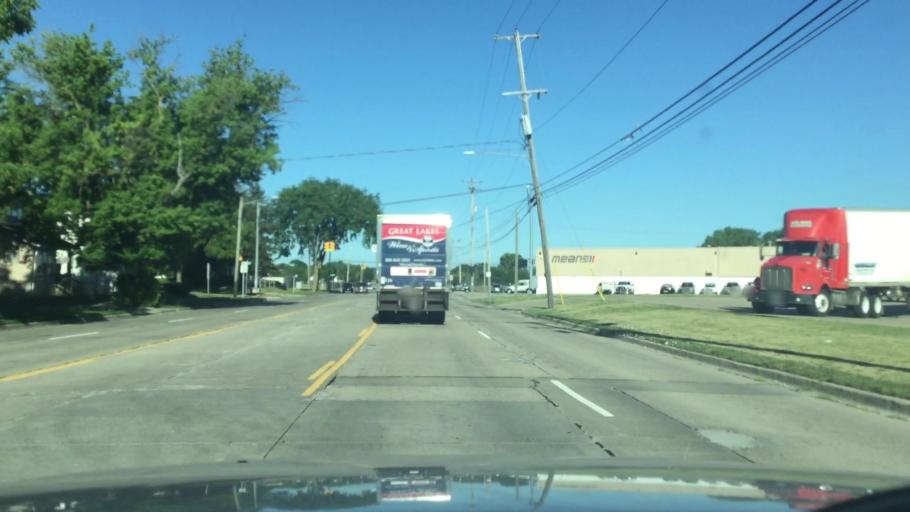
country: US
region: Michigan
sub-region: Saginaw County
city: Saginaw
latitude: 43.4102
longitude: -83.9423
